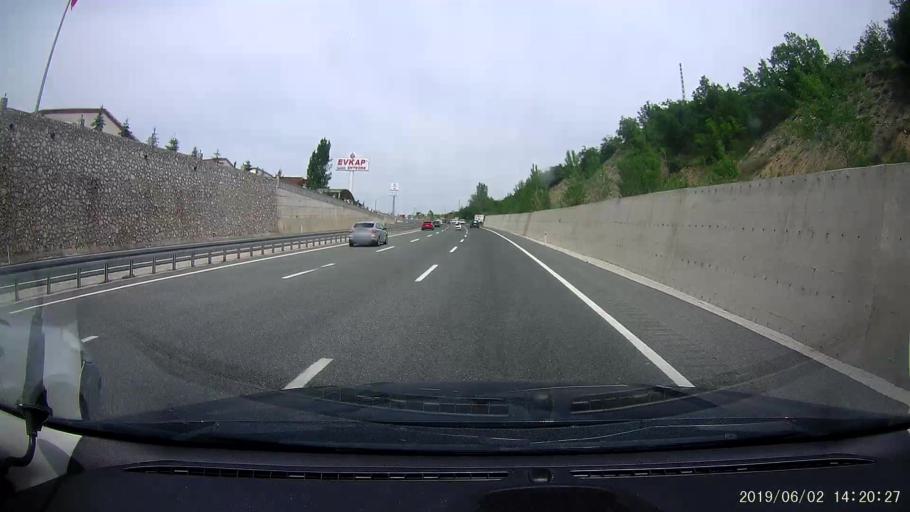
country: TR
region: Kastamonu
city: Tosya
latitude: 40.9698
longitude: 33.9916
